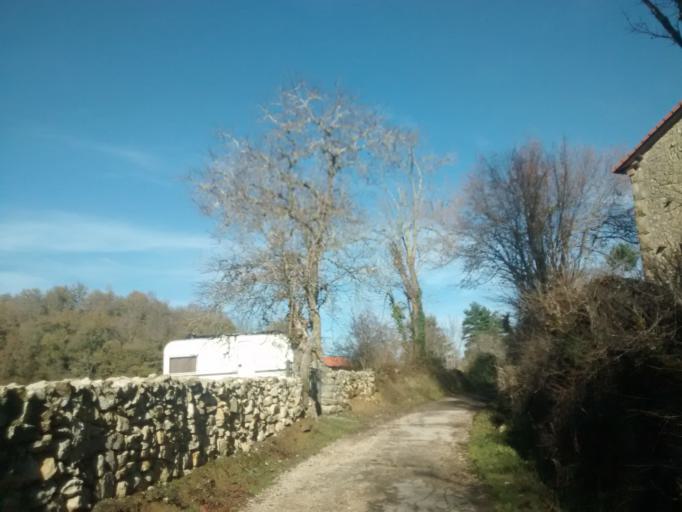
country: ES
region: Cantabria
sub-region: Provincia de Cantabria
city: San Pedro del Romeral
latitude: 42.9645
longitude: -3.7426
